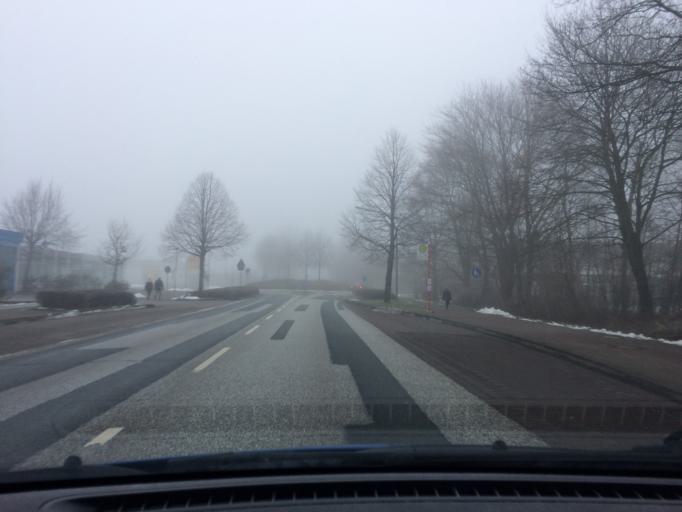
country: DE
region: Schleswig-Holstein
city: Schwarzenbek
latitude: 53.5112
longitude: 10.4893
